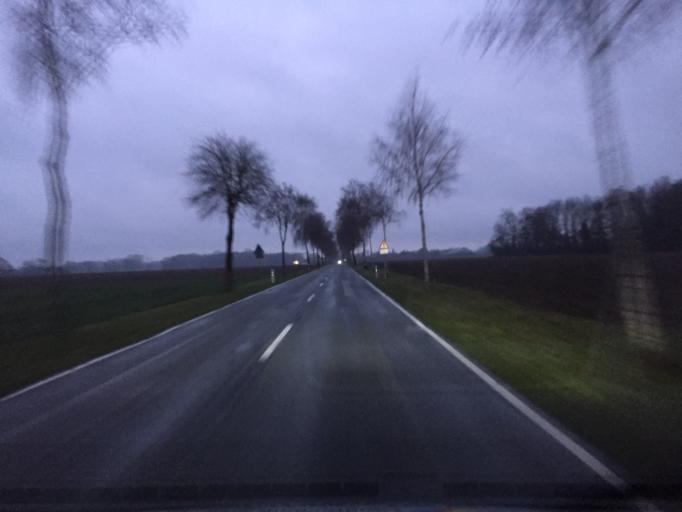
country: DE
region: Lower Saxony
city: Sudwalde
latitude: 52.8054
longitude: 8.8423
